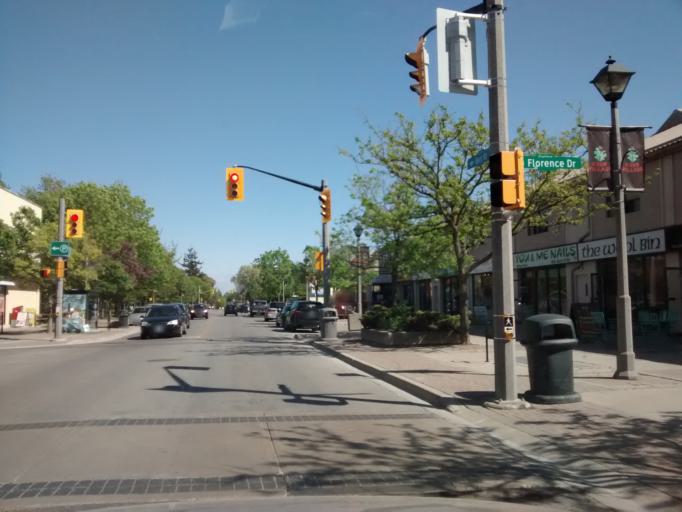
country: CA
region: Ontario
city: Oakville
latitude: 43.4438
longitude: -79.6817
